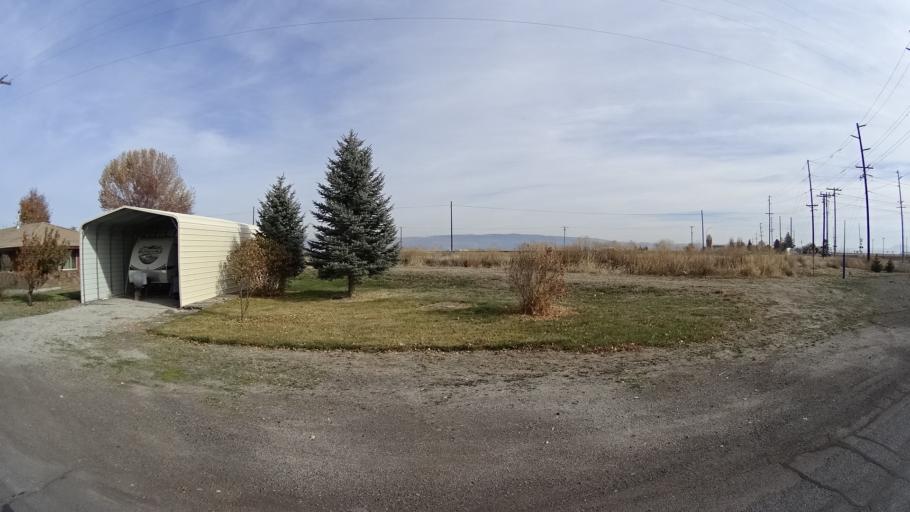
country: US
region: California
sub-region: Siskiyou County
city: Tulelake
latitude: 41.9540
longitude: -121.4723
